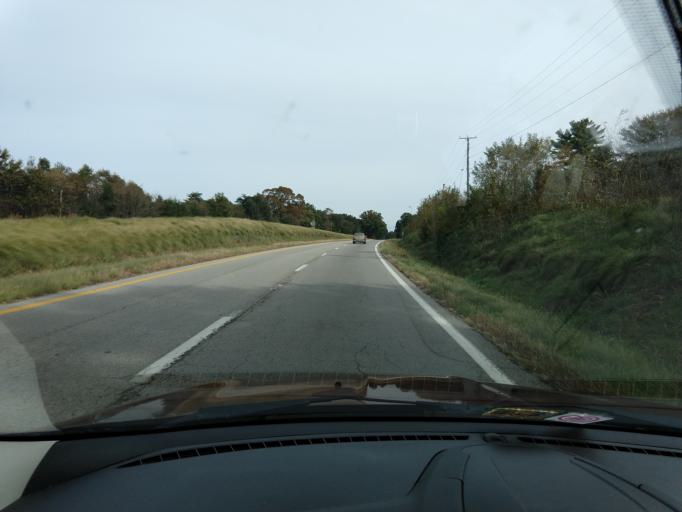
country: US
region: Virginia
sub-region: Pittsylvania County
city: Chatham
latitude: 36.8870
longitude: -79.4047
